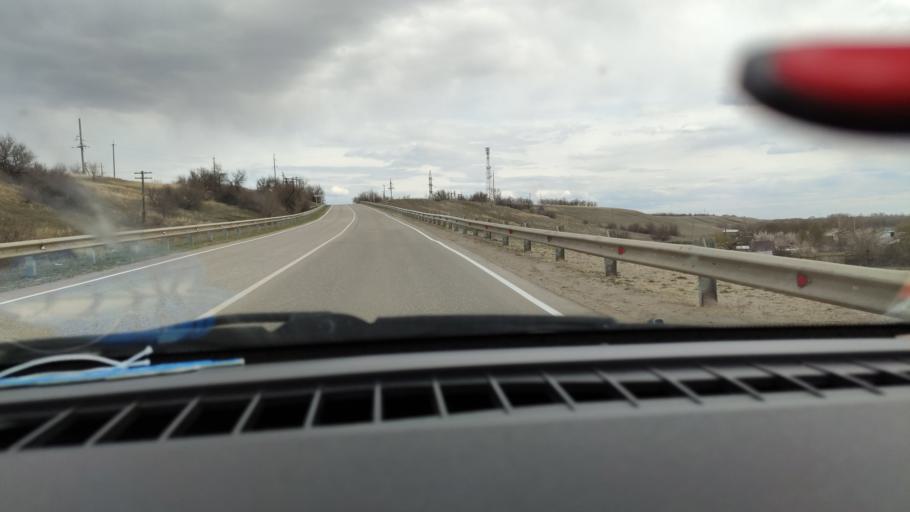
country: RU
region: Saratov
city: Privolzhskiy
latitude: 51.1780
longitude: 45.9250
